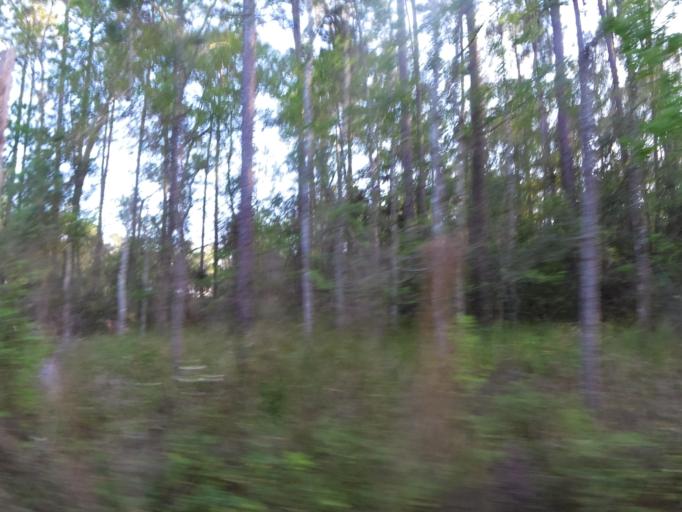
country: US
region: Florida
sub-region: Saint Johns County
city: Fruit Cove
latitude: 30.0674
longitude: -81.5045
